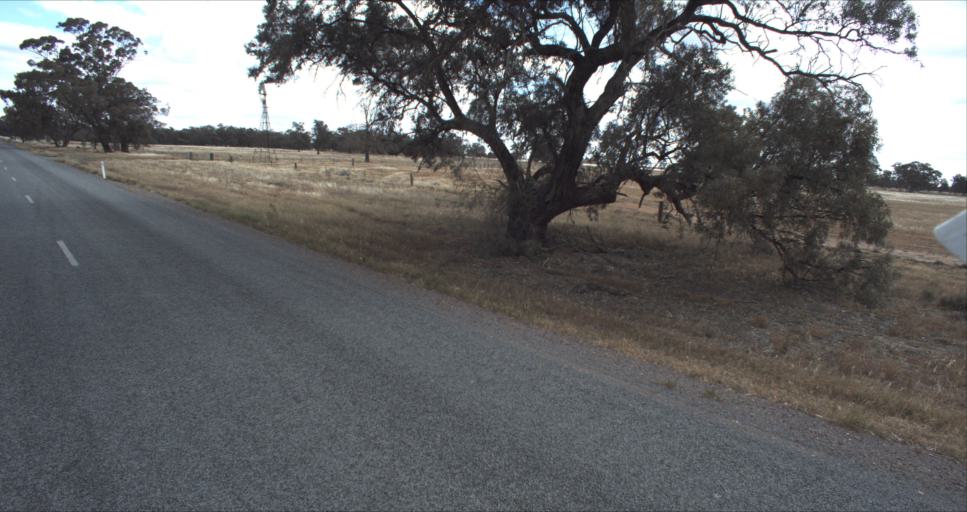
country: AU
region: New South Wales
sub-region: Leeton
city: Leeton
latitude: -34.6857
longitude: 146.3447
